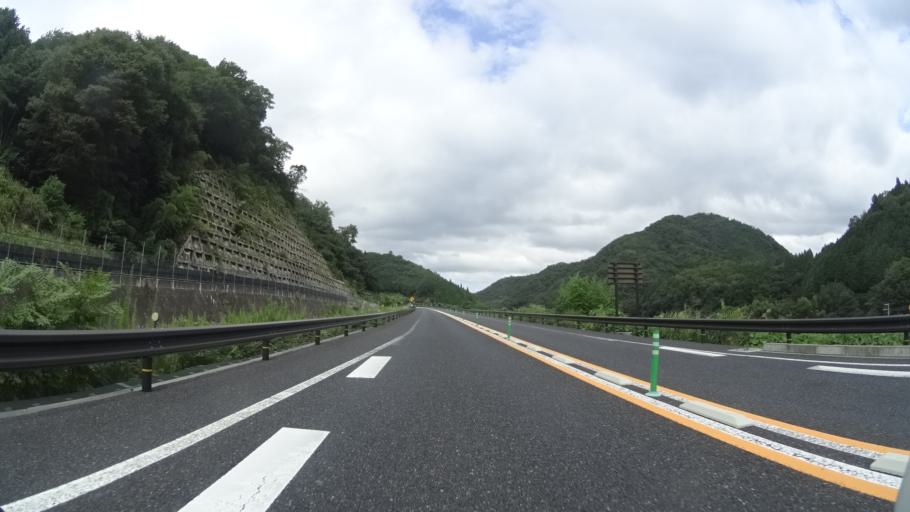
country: JP
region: Hyogo
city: Yamazakicho-nakabirose
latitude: 35.0595
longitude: 134.3648
